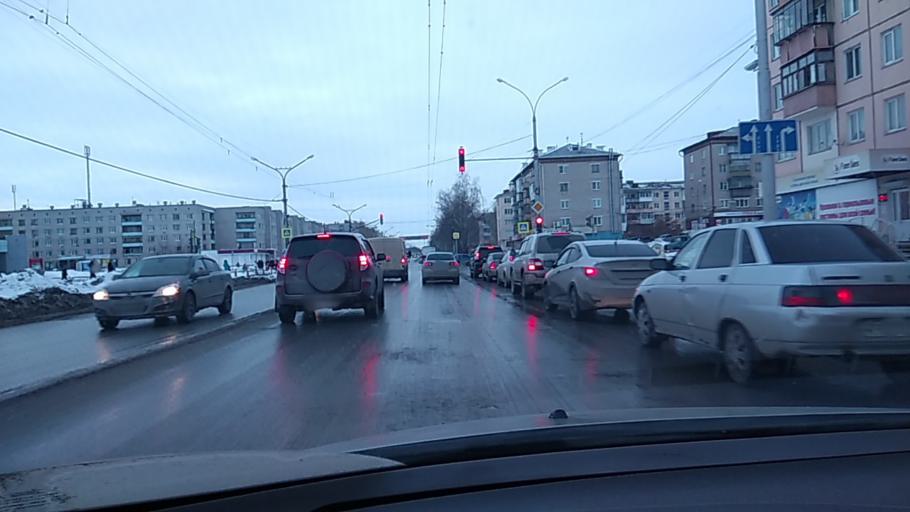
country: RU
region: Sverdlovsk
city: Martyush
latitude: 56.4253
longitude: 61.9014
